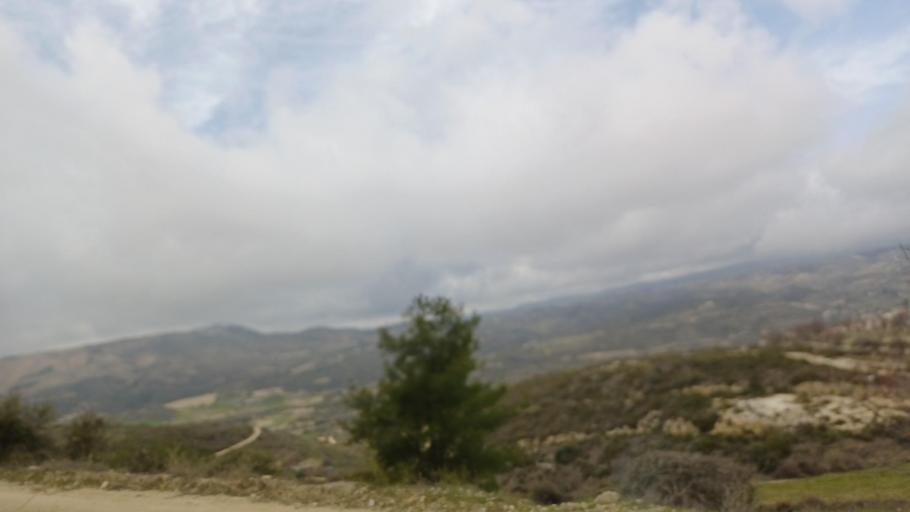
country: CY
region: Limassol
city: Pachna
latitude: 34.7694
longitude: 32.8313
